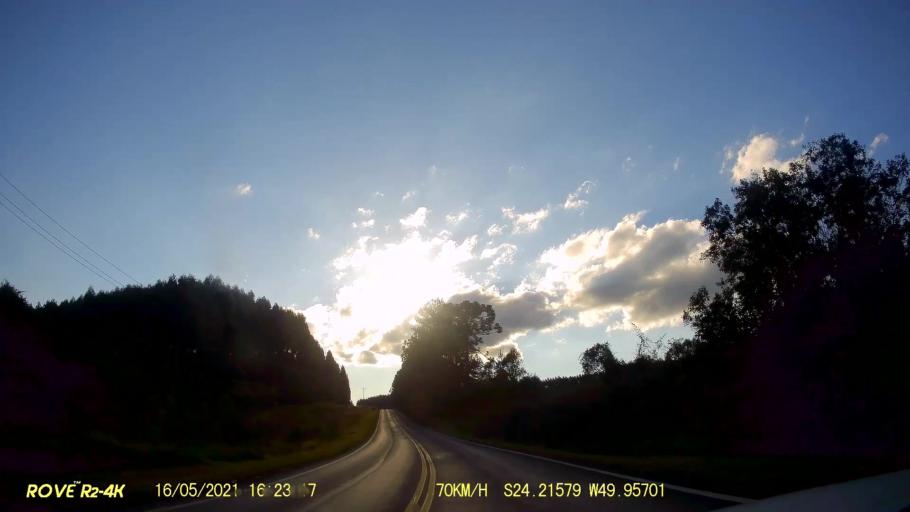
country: BR
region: Parana
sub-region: Jaguariaiva
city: Jaguariaiva
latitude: -24.2157
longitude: -49.9572
